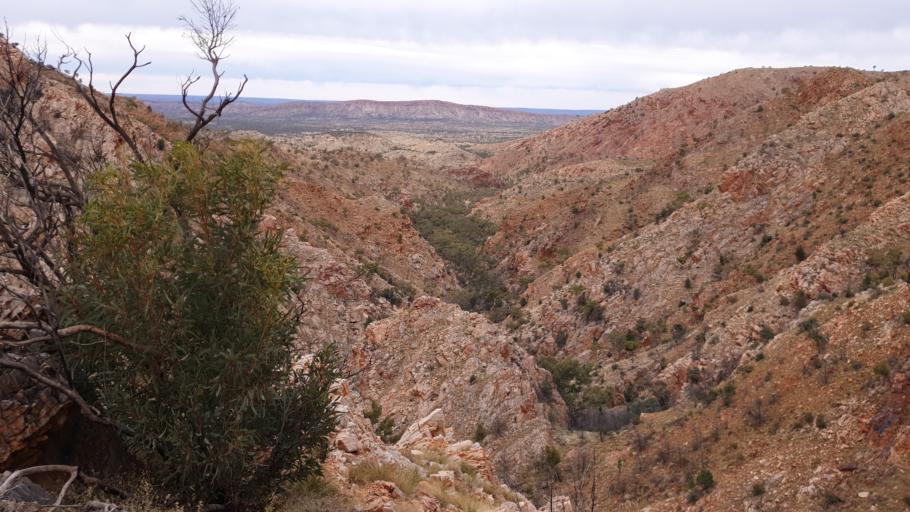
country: AU
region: Northern Territory
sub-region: Alice Springs
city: Alice Springs
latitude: -23.7158
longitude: 133.4695
